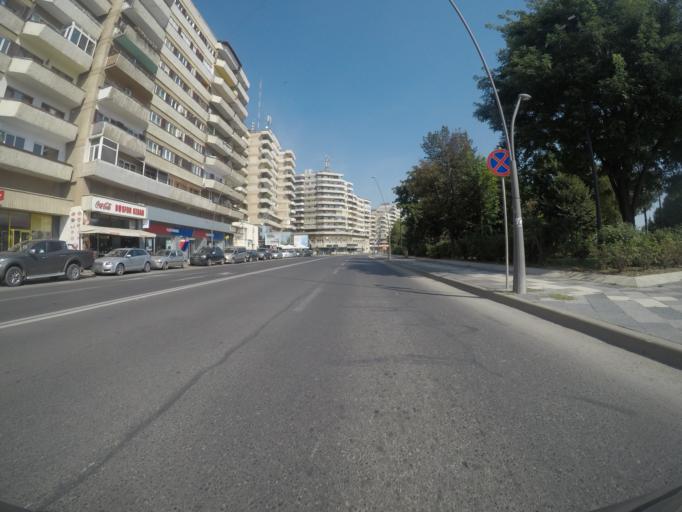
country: RO
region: Alba
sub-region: Municipiul Alba Iulia
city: Alba Iulia
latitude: 46.0682
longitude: 23.5643
